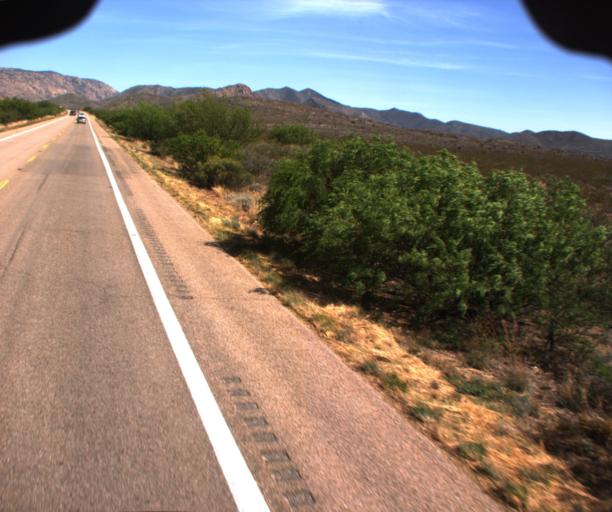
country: US
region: Arizona
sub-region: Cochise County
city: Bisbee
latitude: 31.5287
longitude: -110.0527
